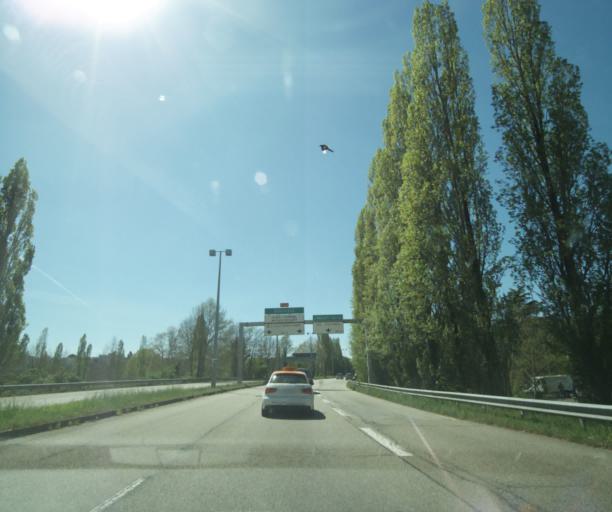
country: FR
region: Limousin
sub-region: Departement de la Haute-Vienne
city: Limoges
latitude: 45.8351
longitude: 1.2775
